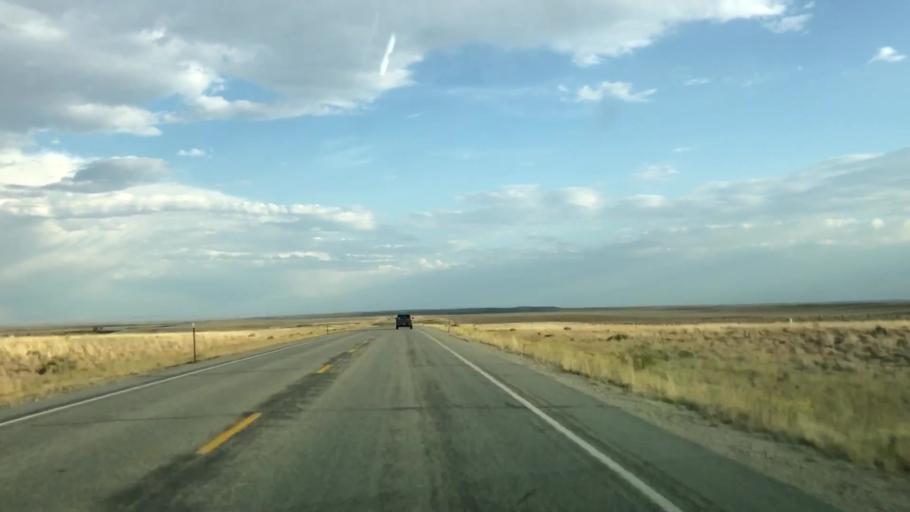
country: US
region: Wyoming
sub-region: Sublette County
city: Marbleton
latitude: 42.3342
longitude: -109.5184
